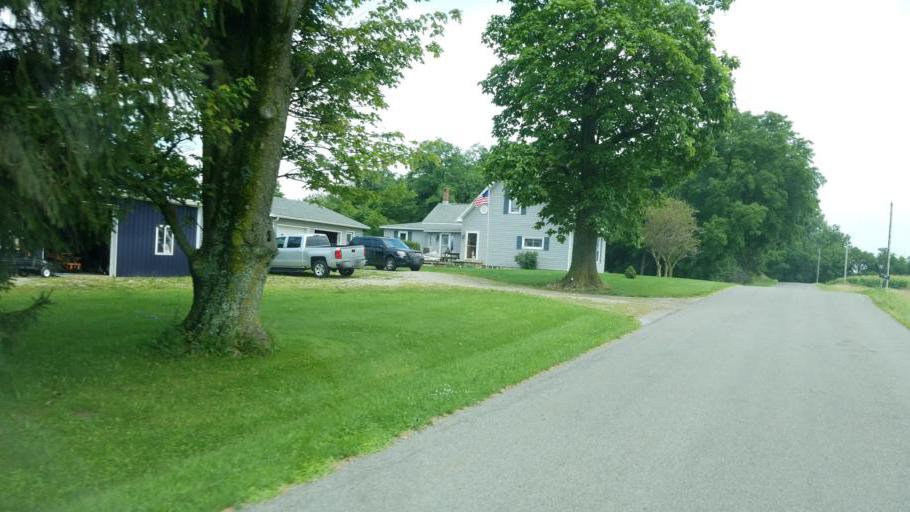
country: US
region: Ohio
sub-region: Logan County
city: Northwood
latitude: 40.4170
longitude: -83.7173
